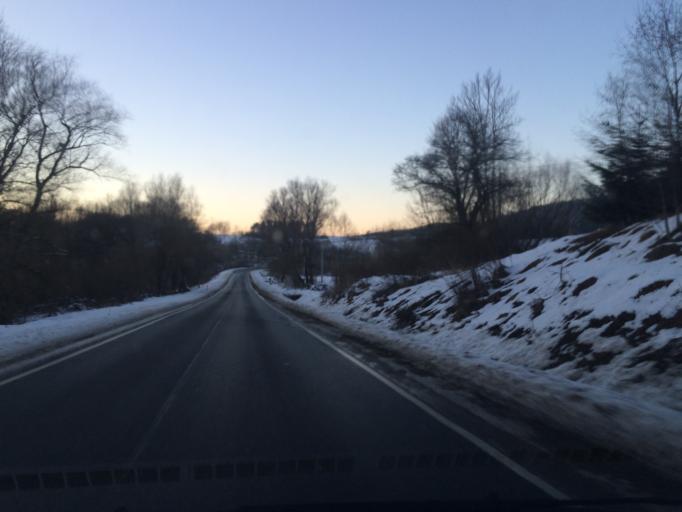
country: PL
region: Subcarpathian Voivodeship
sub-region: Powiat bieszczadzki
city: Czarna
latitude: 49.3817
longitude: 22.6405
